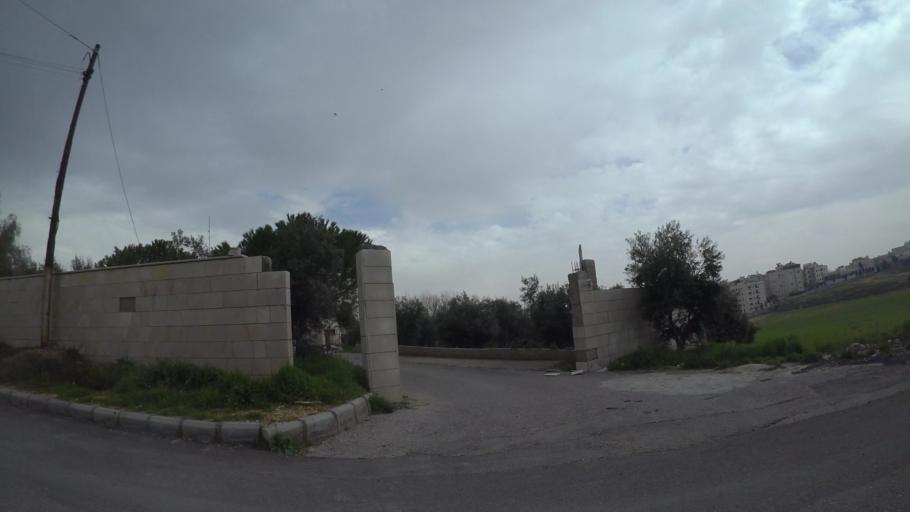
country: JO
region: Amman
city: Umm as Summaq
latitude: 31.9073
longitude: 35.8366
